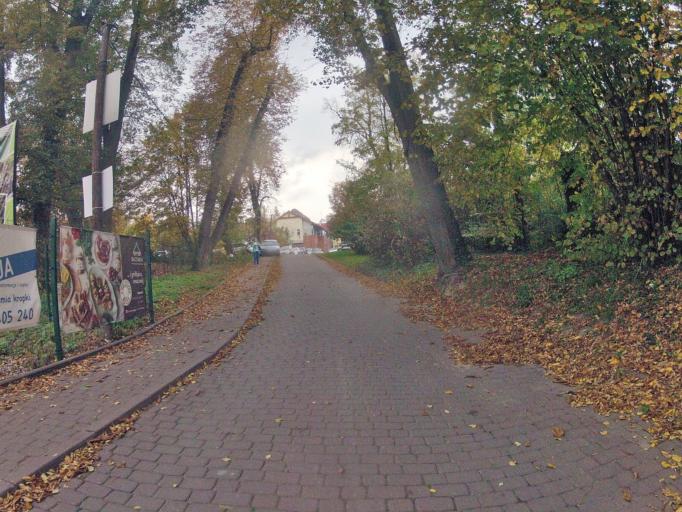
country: PL
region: Lesser Poland Voivodeship
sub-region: Powiat krakowski
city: Rzaska
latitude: 50.0646
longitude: 19.8695
